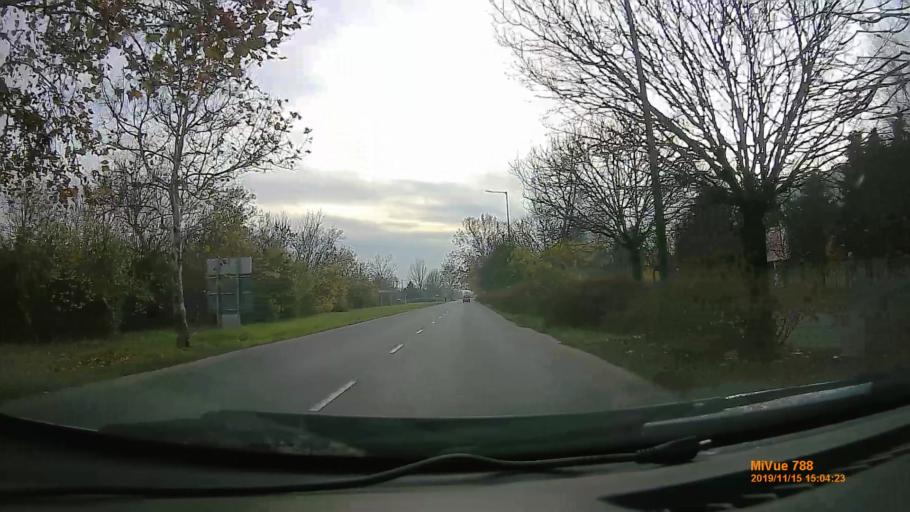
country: HU
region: Bekes
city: Gyula
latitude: 46.6381
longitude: 21.2618
